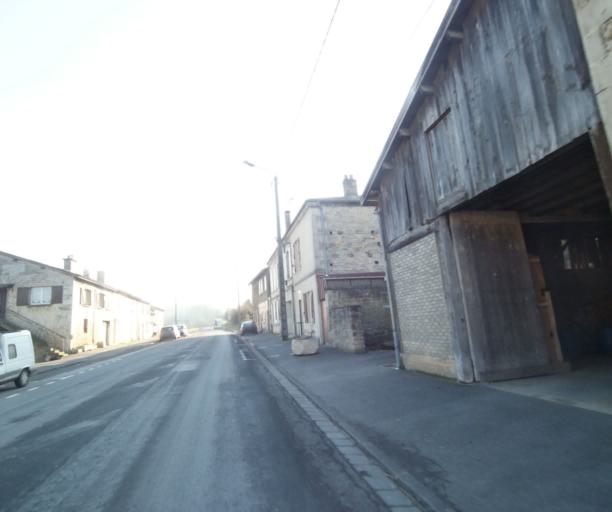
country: FR
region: Champagne-Ardenne
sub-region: Departement de la Haute-Marne
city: Chevillon
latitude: 48.5232
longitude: 5.1039
